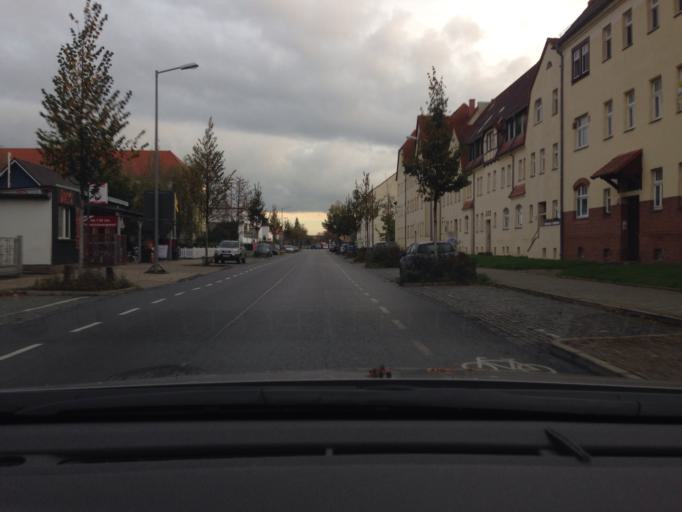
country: DE
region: Saxony
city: Taucha
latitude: 51.3367
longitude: 12.4729
